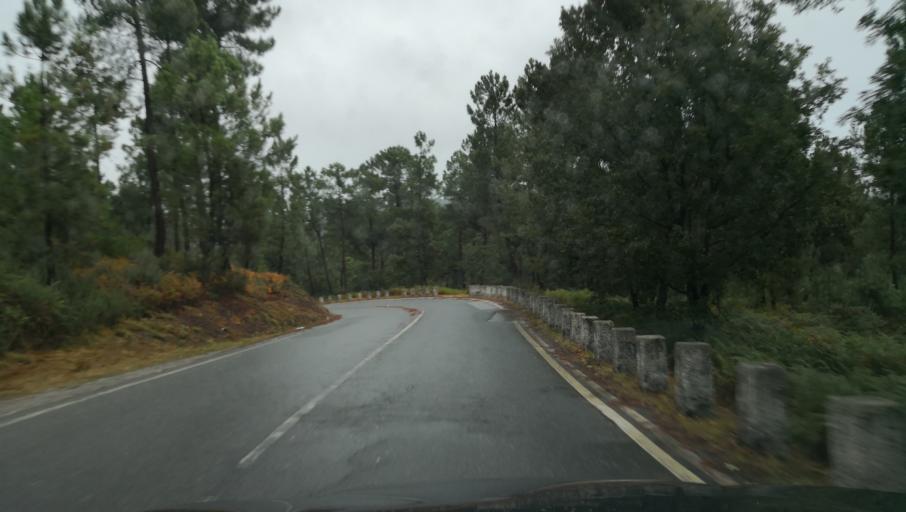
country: PT
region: Vila Real
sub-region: Sabrosa
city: Sabrosa
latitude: 41.3474
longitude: -7.5929
